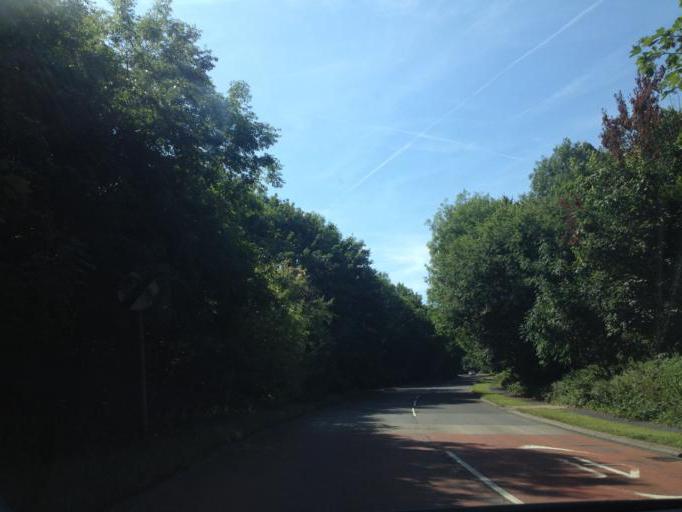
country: GB
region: England
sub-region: Hertfordshire
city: Welwyn
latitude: 51.8213
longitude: -0.2163
